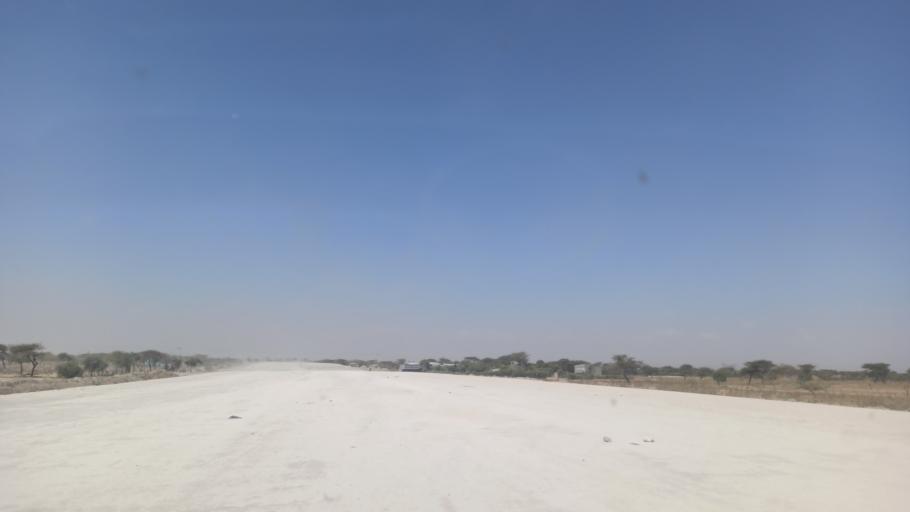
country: ET
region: Oromiya
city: Ziway
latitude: 7.6902
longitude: 38.6618
